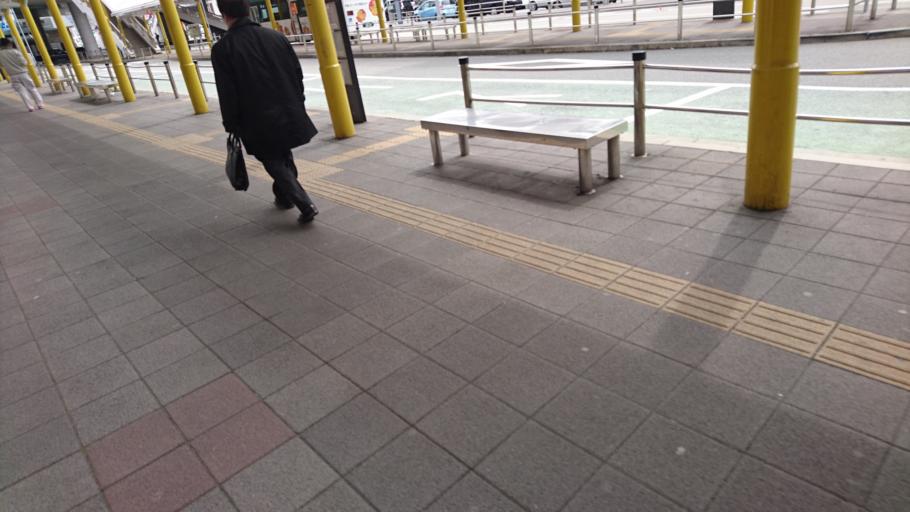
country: JP
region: Hyogo
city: Sandacho
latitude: 34.8885
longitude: 135.2289
